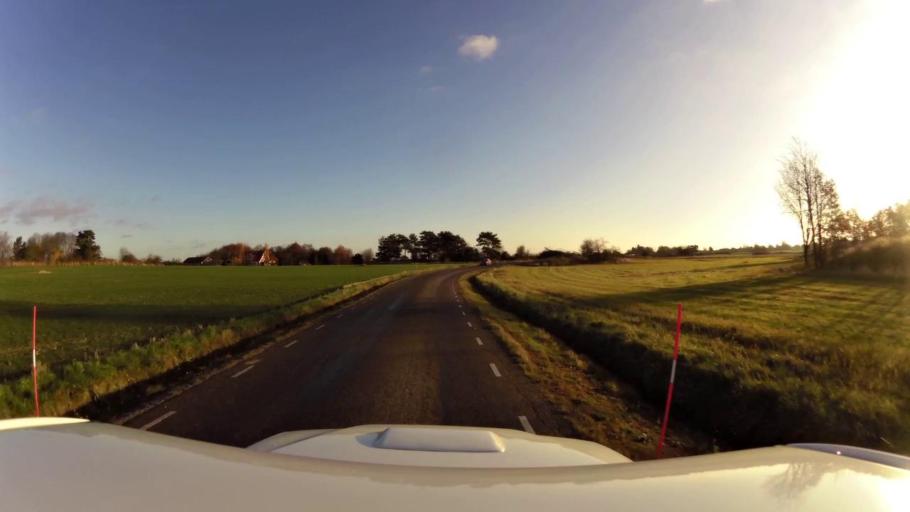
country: SE
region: OEstergoetland
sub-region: Linkopings Kommun
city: Linghem
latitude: 58.4822
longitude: 15.7331
